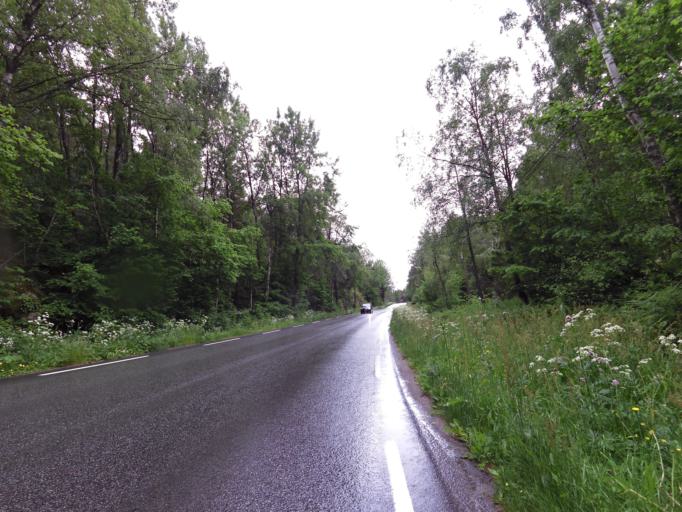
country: NO
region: Vest-Agder
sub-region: Mandal
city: Mandal
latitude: 58.0236
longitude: 7.5171
